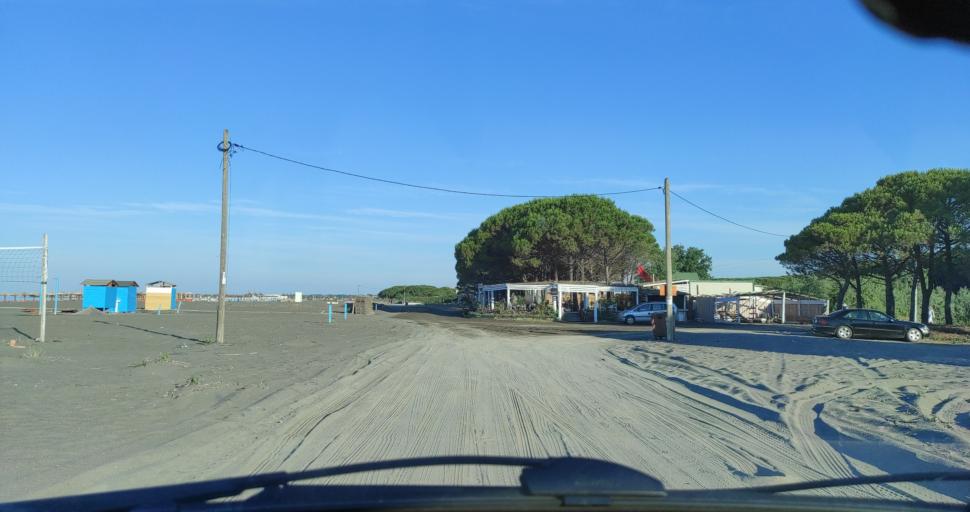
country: AL
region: Shkoder
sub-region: Rrethi i Shkodres
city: Velipoje
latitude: 41.8599
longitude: 19.4402
